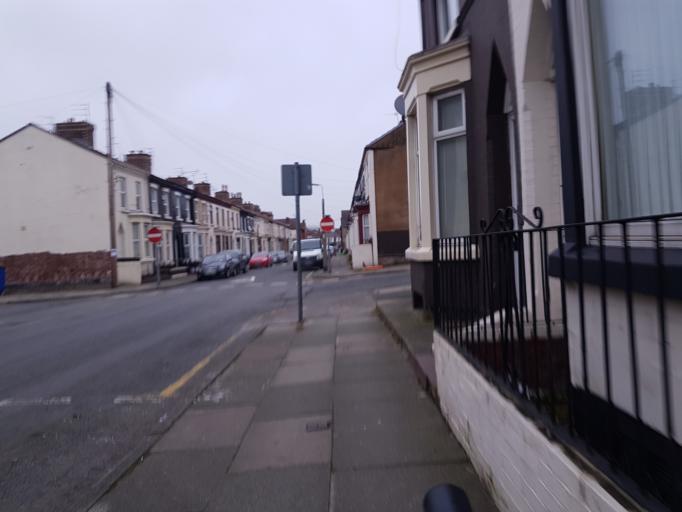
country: GB
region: England
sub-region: Sefton
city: Litherland
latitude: 53.4469
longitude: -2.9721
